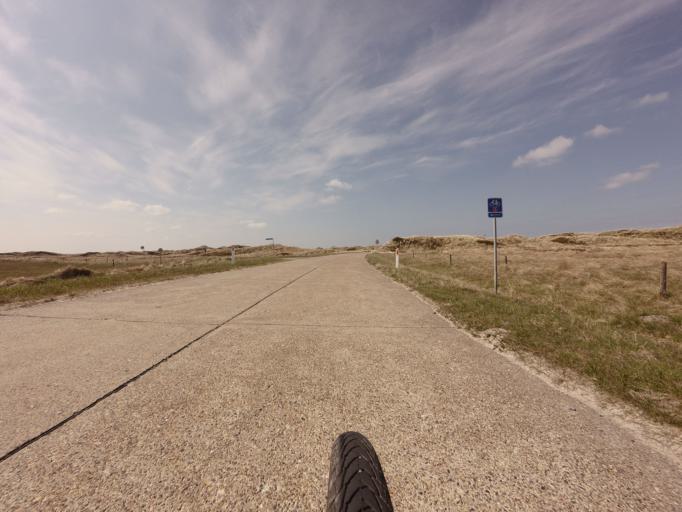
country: DK
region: North Denmark
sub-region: Jammerbugt Kommune
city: Brovst
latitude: 57.1765
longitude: 9.4403
